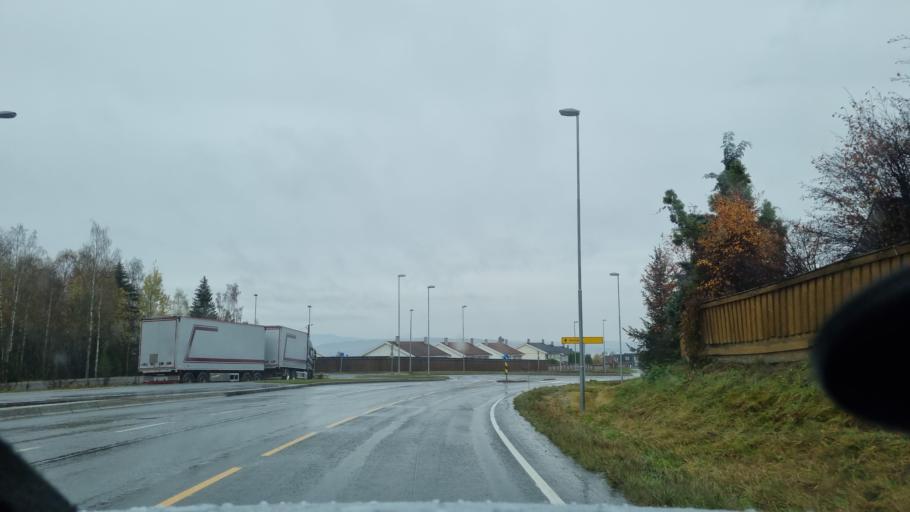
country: NO
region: Hedmark
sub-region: Hamar
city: Hamar
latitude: 60.8157
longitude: 11.0645
